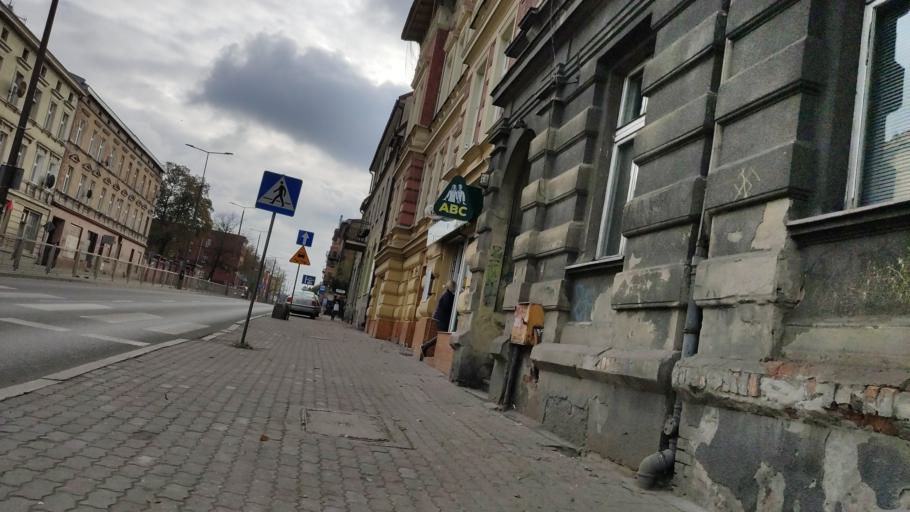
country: PL
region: Kujawsko-Pomorskie
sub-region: Powiat inowroclawski
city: Inowroclaw
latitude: 52.8053
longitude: 18.2476
